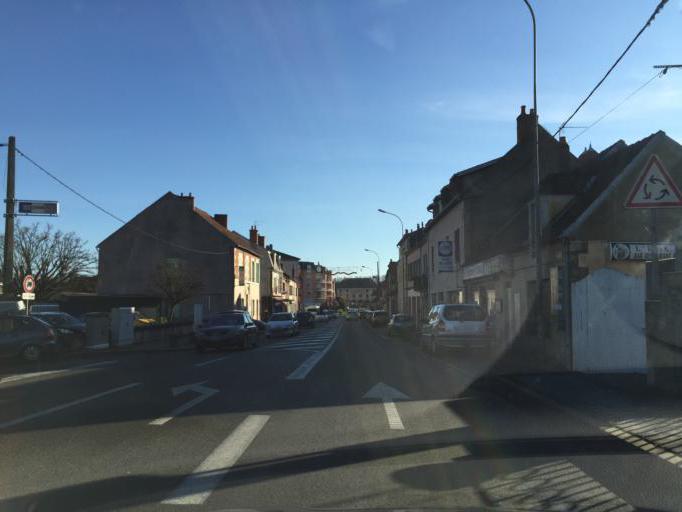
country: FR
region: Auvergne
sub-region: Departement de l'Allier
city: Saint-Pourcain-sur-Sioule
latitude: 46.3063
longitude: 3.2953
